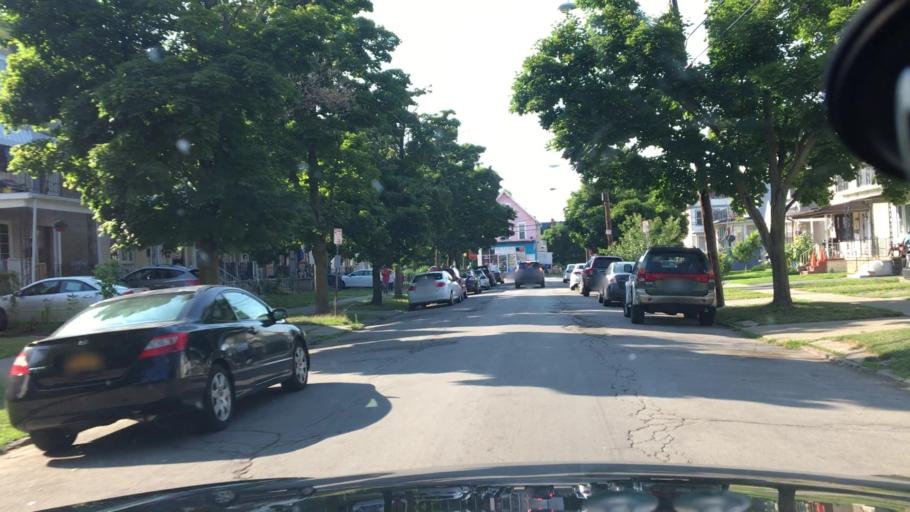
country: US
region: New York
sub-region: Erie County
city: Buffalo
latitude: 42.9108
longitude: -78.8943
